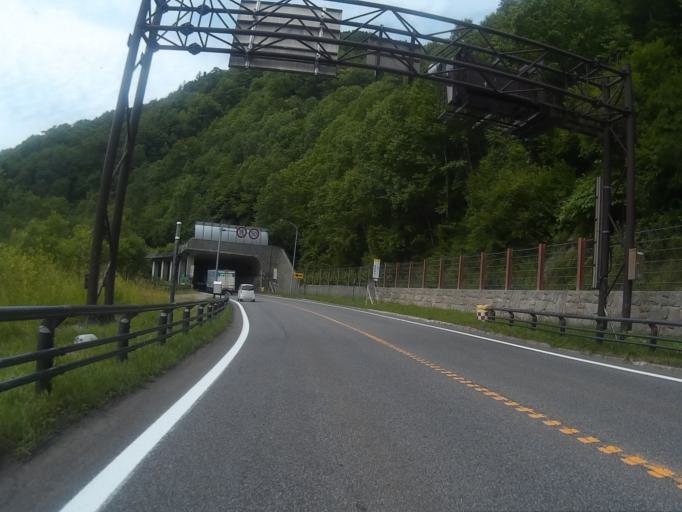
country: JP
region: Hokkaido
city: Sapporo
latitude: 42.8993
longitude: 141.1301
